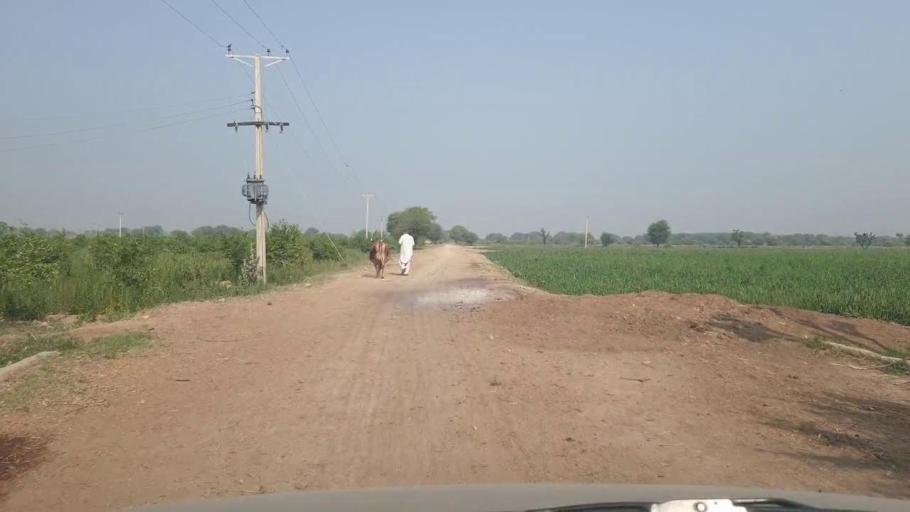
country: PK
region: Sindh
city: Umarkot
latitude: 25.3897
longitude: 69.7113
